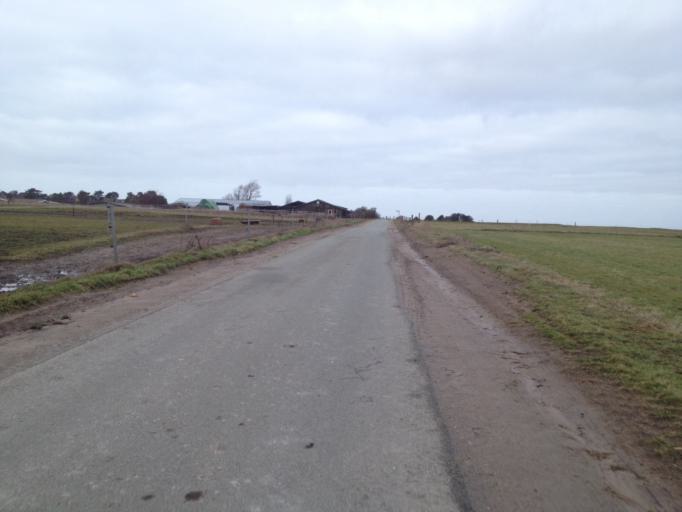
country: DE
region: Schleswig-Holstein
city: Norddorf
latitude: 54.6740
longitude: 8.3412
